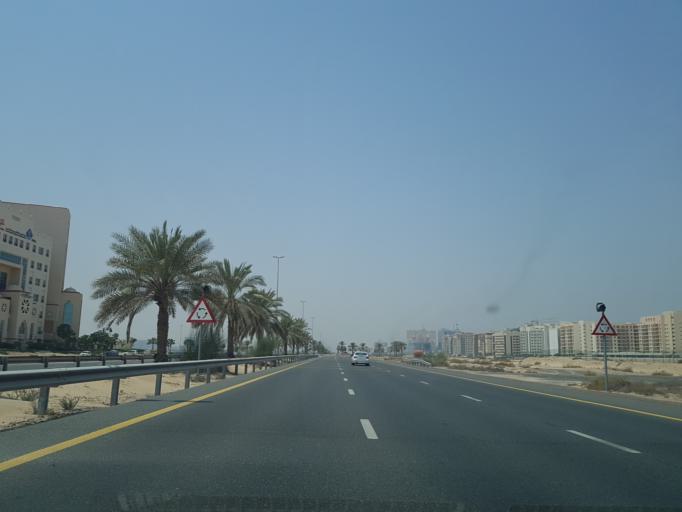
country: AE
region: Ash Shariqah
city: Sharjah
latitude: 25.1270
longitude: 55.4107
